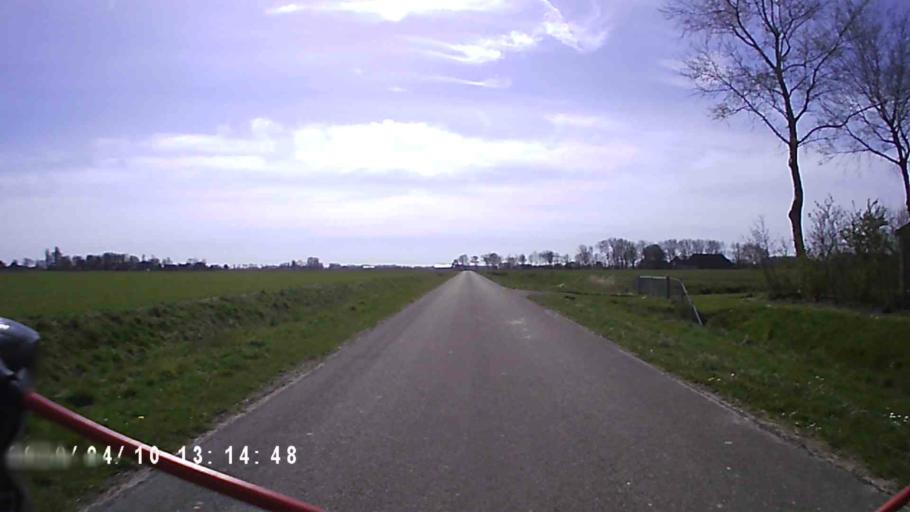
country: NL
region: Groningen
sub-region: Gemeente De Marne
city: Ulrum
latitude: 53.3990
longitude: 6.4171
